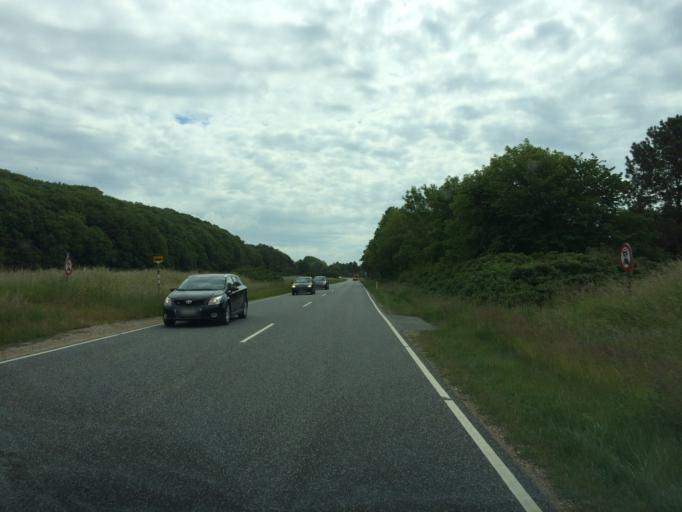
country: DK
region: Zealand
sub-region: Odsherred Kommune
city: Hojby
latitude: 55.9557
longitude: 11.4731
